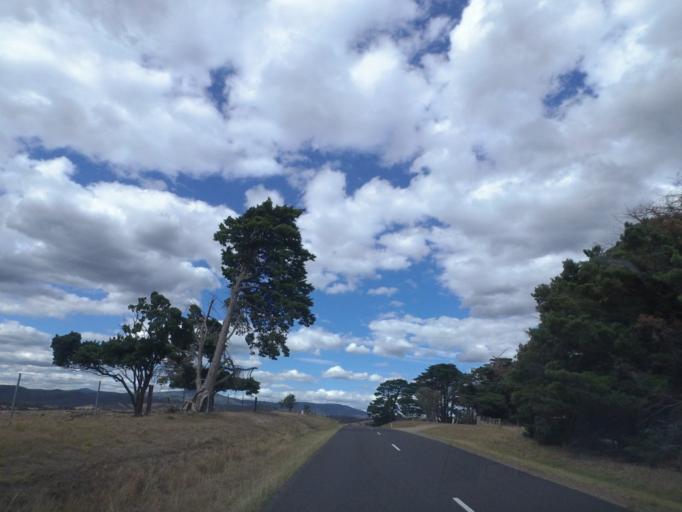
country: AU
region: Victoria
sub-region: Yarra Ranges
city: Yarra Glen
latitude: -37.6399
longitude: 145.4249
